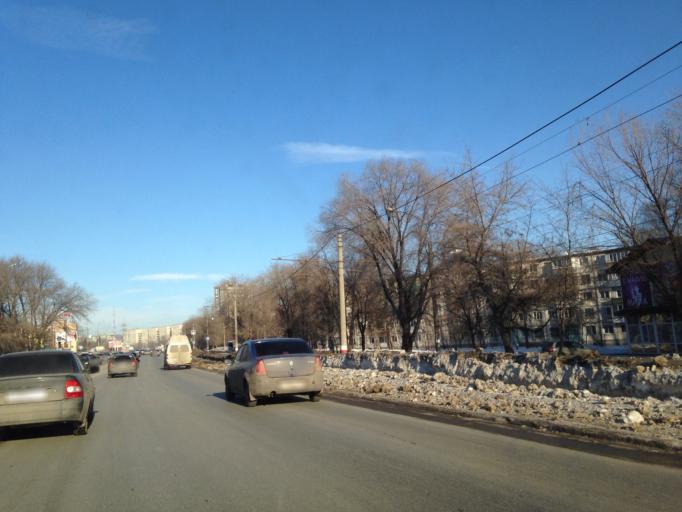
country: RU
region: Ulyanovsk
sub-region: Ulyanovskiy Rayon
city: Ulyanovsk
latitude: 54.3107
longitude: 48.3510
